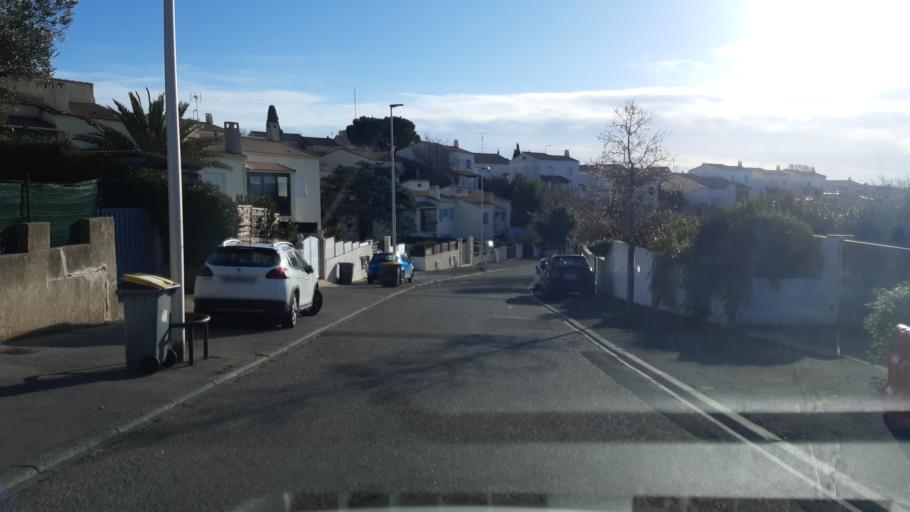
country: FR
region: Languedoc-Roussillon
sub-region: Departement de l'Herault
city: Grabels
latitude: 43.6384
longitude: 3.8108
